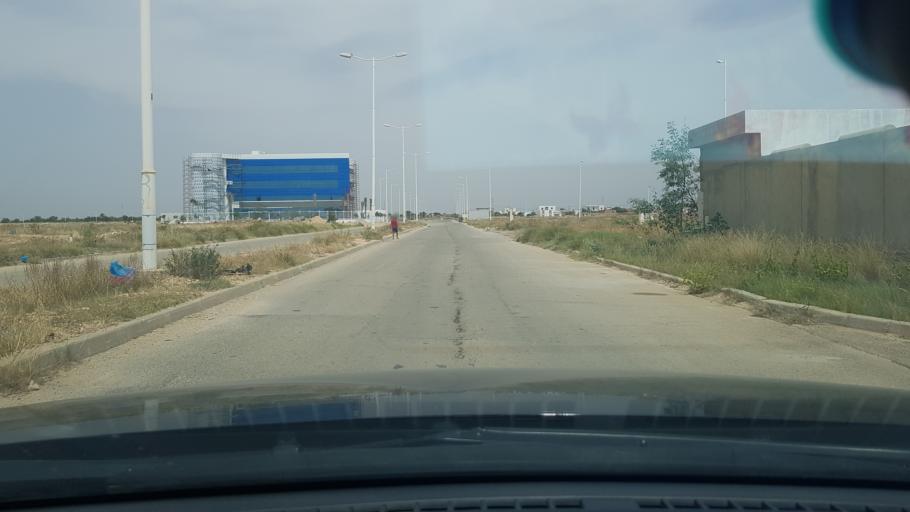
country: TN
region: Safaqis
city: Al Qarmadah
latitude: 34.8307
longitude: 10.7488
